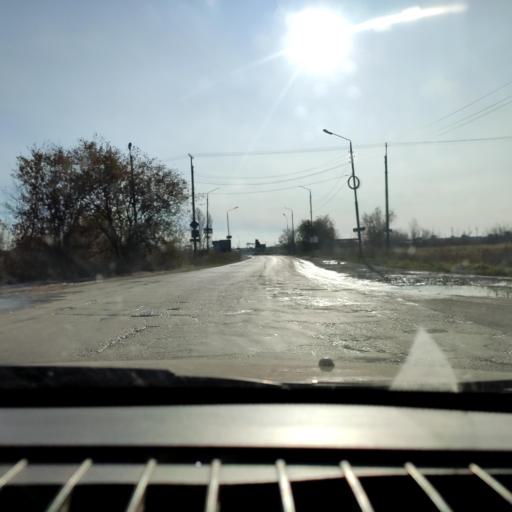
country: RU
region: Samara
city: Tol'yatti
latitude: 53.5742
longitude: 49.3399
